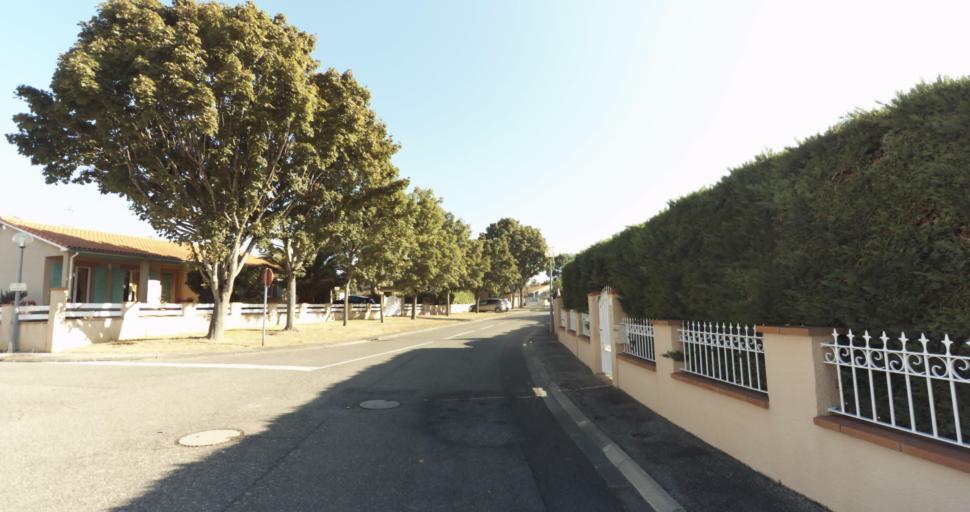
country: FR
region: Midi-Pyrenees
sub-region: Departement de la Haute-Garonne
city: L'Union
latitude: 43.6626
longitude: 1.4890
